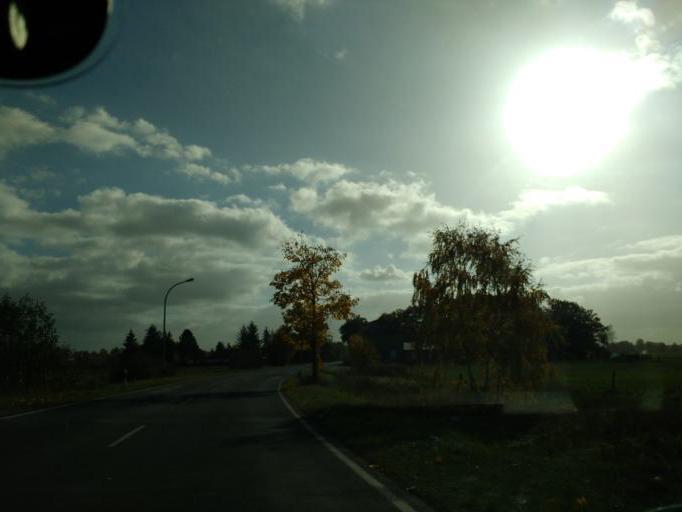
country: DE
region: Brandenburg
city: Spreenhagen
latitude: 52.3654
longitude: 13.8398
